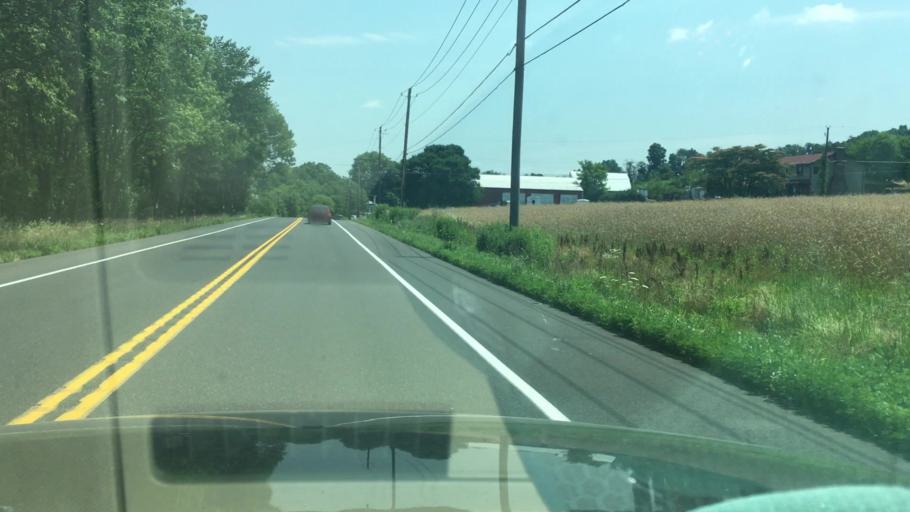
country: US
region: Pennsylvania
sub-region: Lehigh County
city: Schnecksville
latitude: 40.6800
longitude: -75.7085
